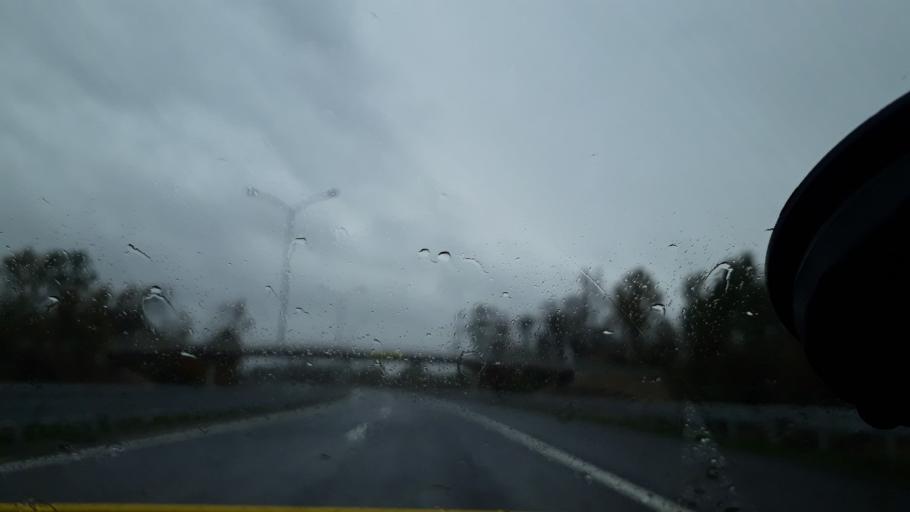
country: BA
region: Republika Srpska
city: Maglajani
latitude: 44.8946
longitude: 17.3660
